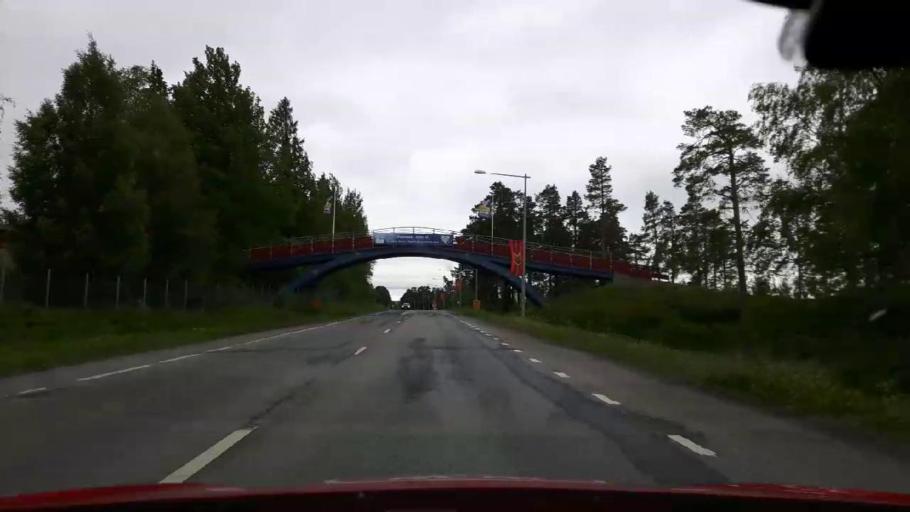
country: SE
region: Jaemtland
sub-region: OEstersunds Kommun
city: Ostersund
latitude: 63.1899
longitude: 14.6545
